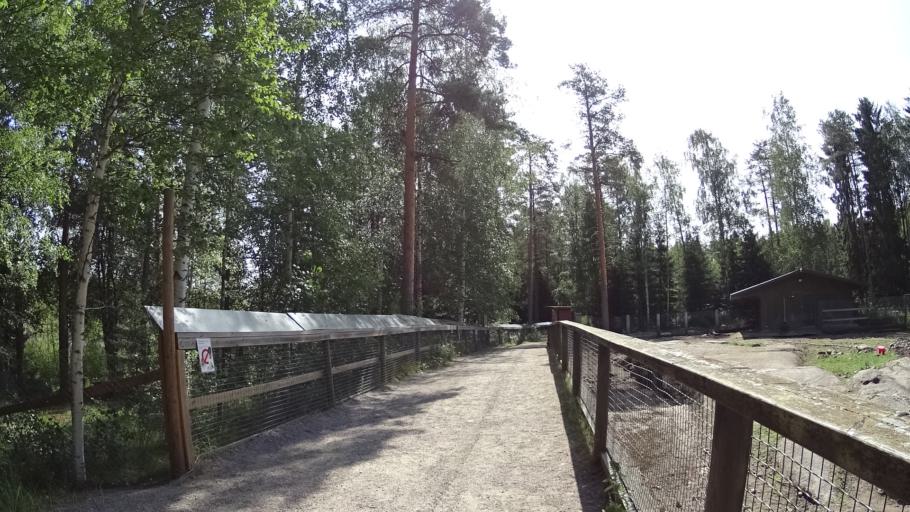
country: FI
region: Southern Ostrobothnia
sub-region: Kuusiokunnat
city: AEhtaeri
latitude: 62.5408
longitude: 24.1800
